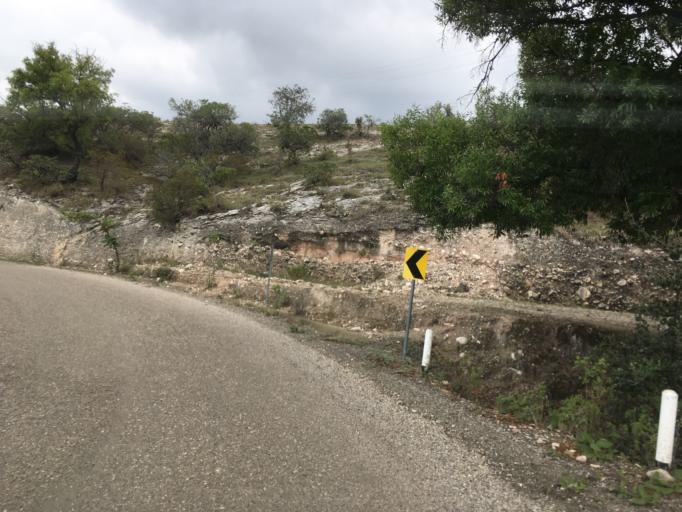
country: MX
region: Oaxaca
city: Santiago Tilantongo
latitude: 17.2415
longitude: -97.2859
